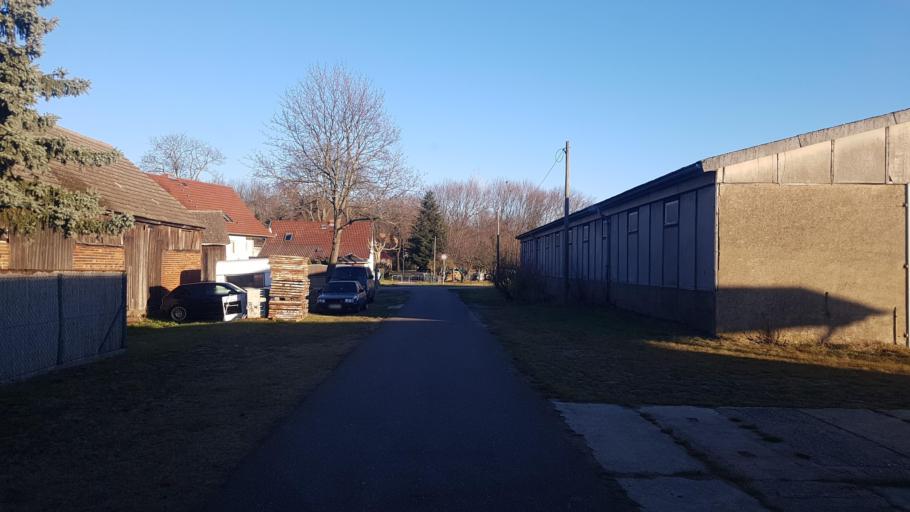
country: DE
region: Brandenburg
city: Tauer
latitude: 51.8984
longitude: 14.4668
